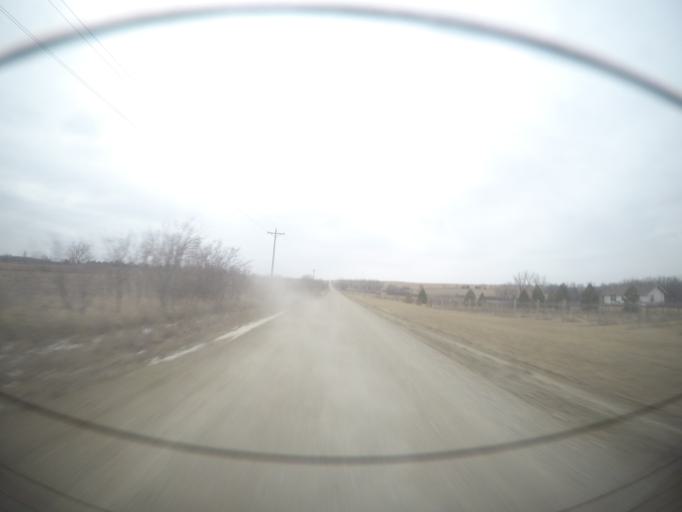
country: US
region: Kansas
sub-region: Pottawatomie County
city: Wamego
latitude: 39.1517
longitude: -96.2449
